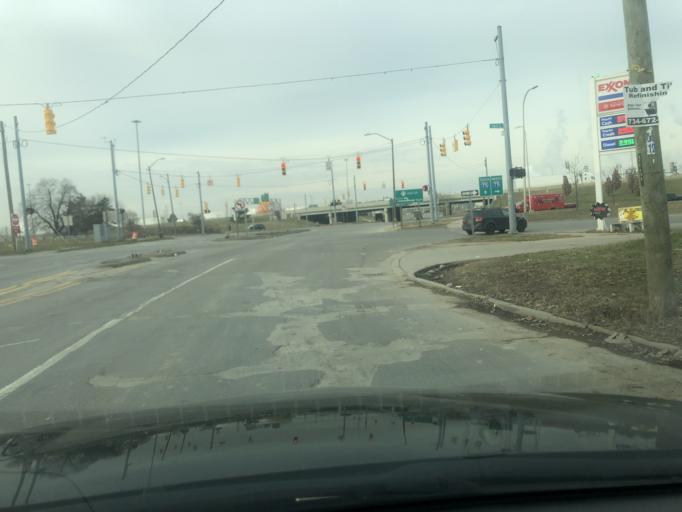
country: US
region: Michigan
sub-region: Wayne County
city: River Rouge
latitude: 42.2760
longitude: -83.1547
